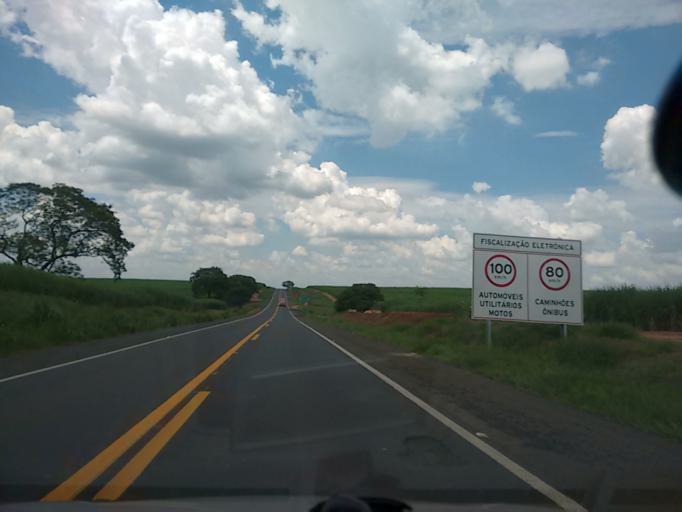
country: BR
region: Sao Paulo
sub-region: Osvaldo Cruz
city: Osvaldo Cruz
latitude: -21.9056
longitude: -50.8866
